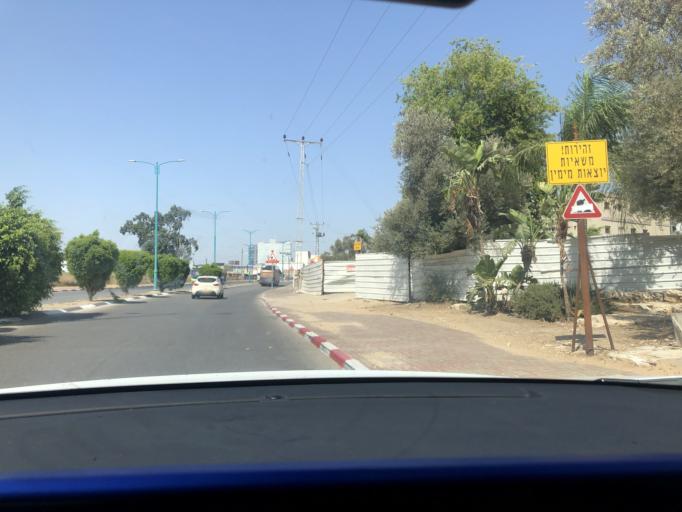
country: IL
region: Central District
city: Ramla
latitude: 31.9433
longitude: 34.8733
